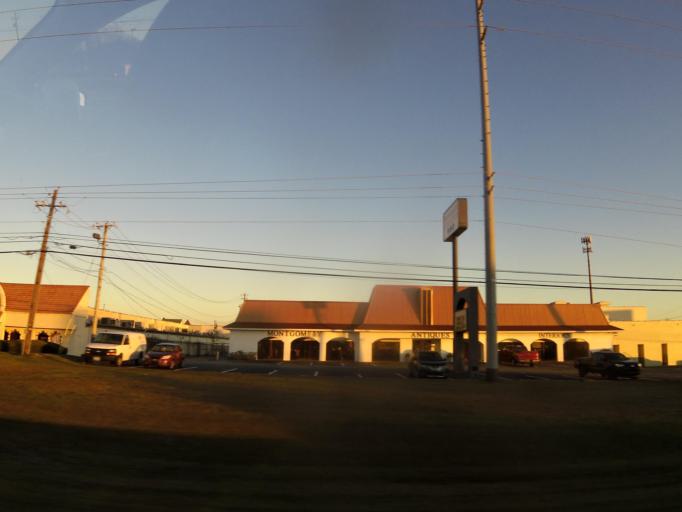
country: US
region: Alabama
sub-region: Montgomery County
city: Montgomery
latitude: 32.3544
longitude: -86.2181
